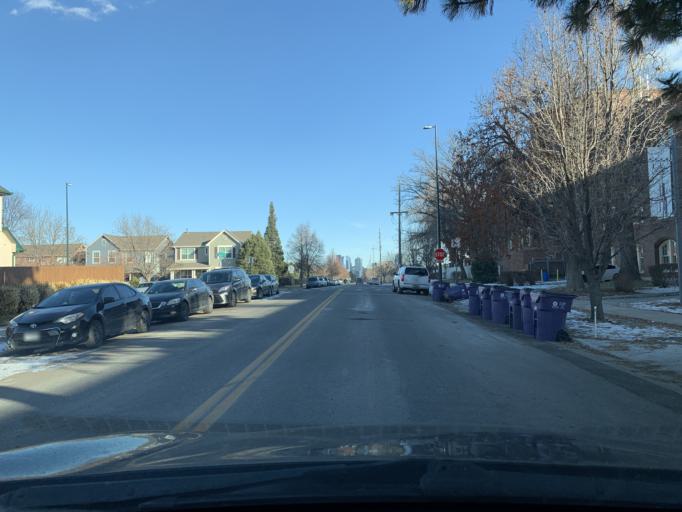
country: US
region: Colorado
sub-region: Jefferson County
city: Edgewater
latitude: 39.7464
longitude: -105.0352
